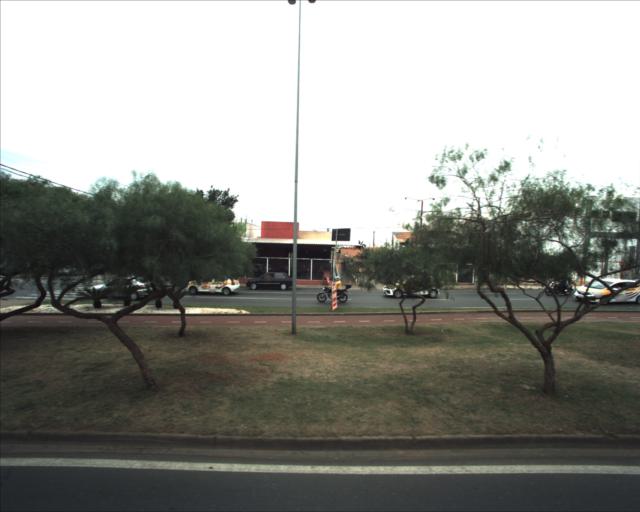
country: BR
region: Sao Paulo
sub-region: Sorocaba
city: Sorocaba
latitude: -23.4915
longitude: -47.5056
